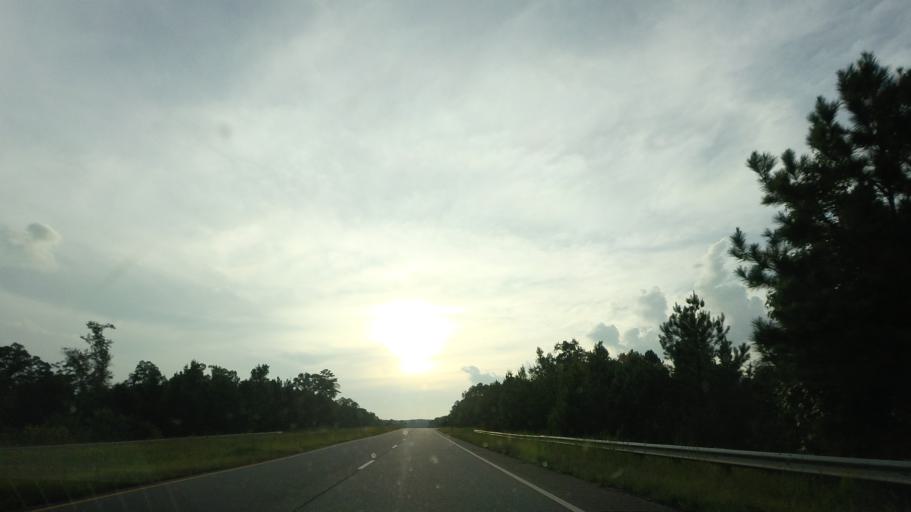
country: US
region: Georgia
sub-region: Wilkinson County
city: Gordon
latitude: 32.8480
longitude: -83.4425
